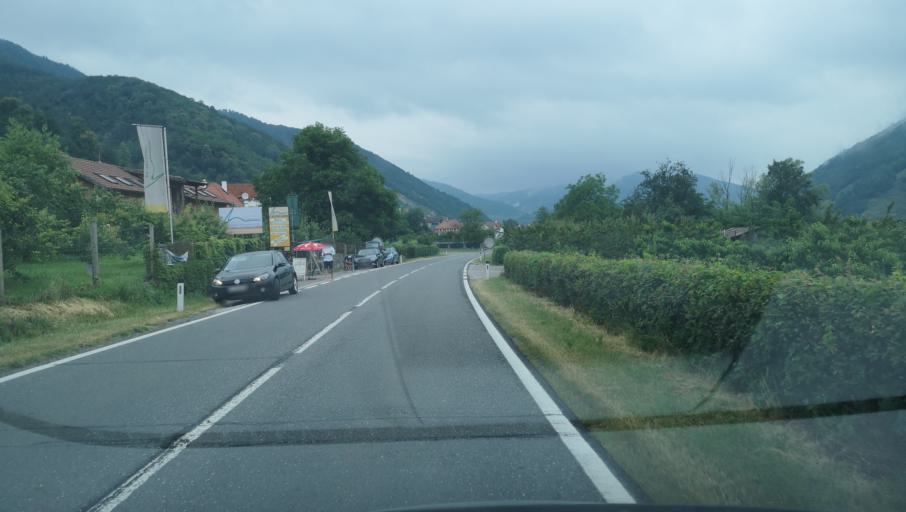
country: AT
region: Lower Austria
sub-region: Politischer Bezirk Krems
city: Spitz
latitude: 48.3367
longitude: 15.4040
